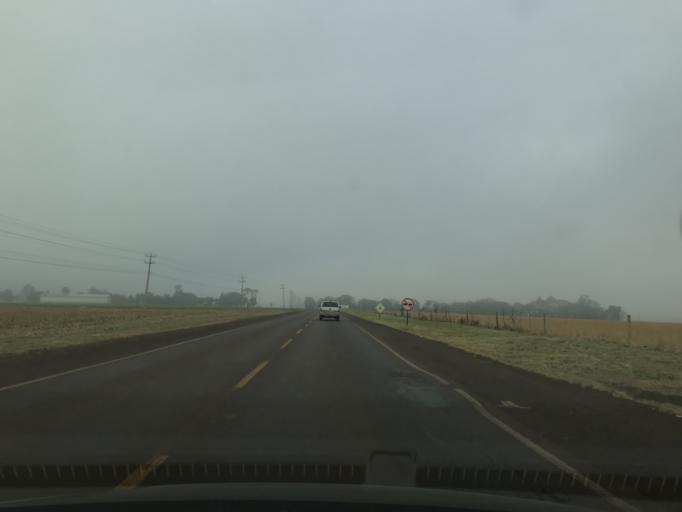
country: BR
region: Parana
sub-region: Toledo
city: Toledo
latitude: -24.6948
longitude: -53.6966
